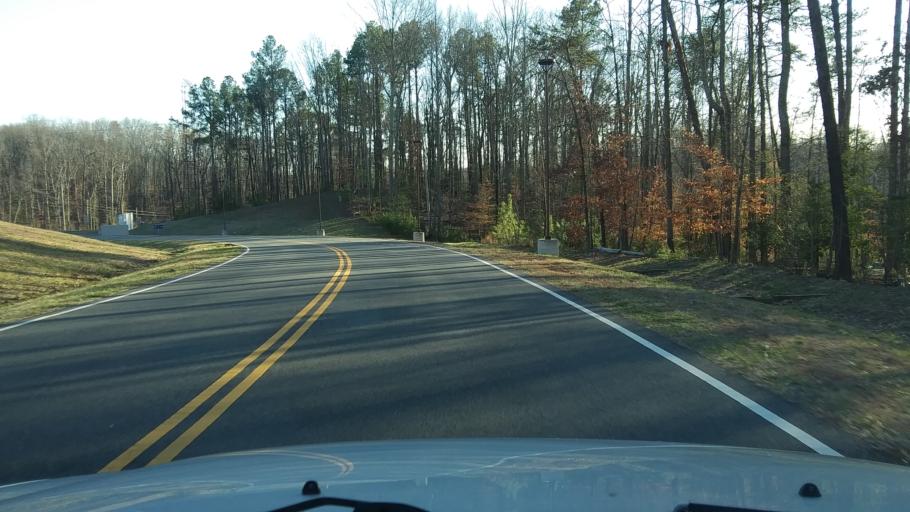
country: US
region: Virginia
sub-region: Prince William County
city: Triangle
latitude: 38.5407
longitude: -77.3425
